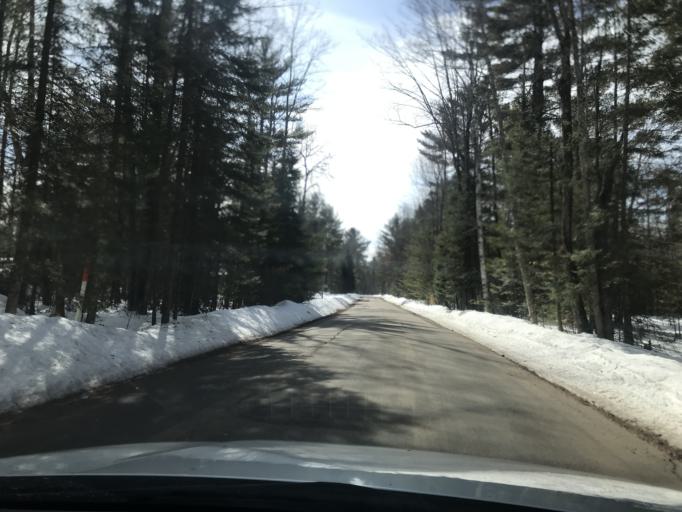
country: US
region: Wisconsin
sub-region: Menominee County
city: Legend Lake
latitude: 45.1200
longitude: -88.4463
